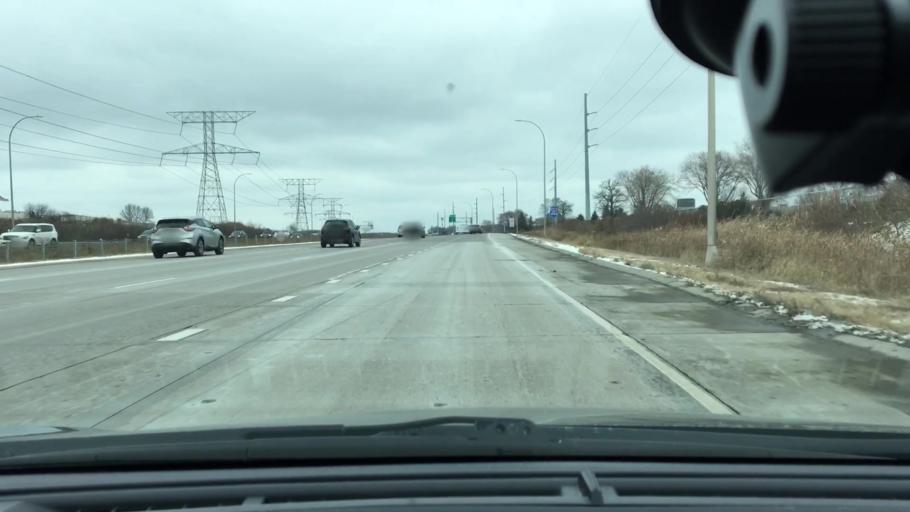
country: US
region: Minnesota
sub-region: Hennepin County
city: Plymouth
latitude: 45.0002
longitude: -93.4574
